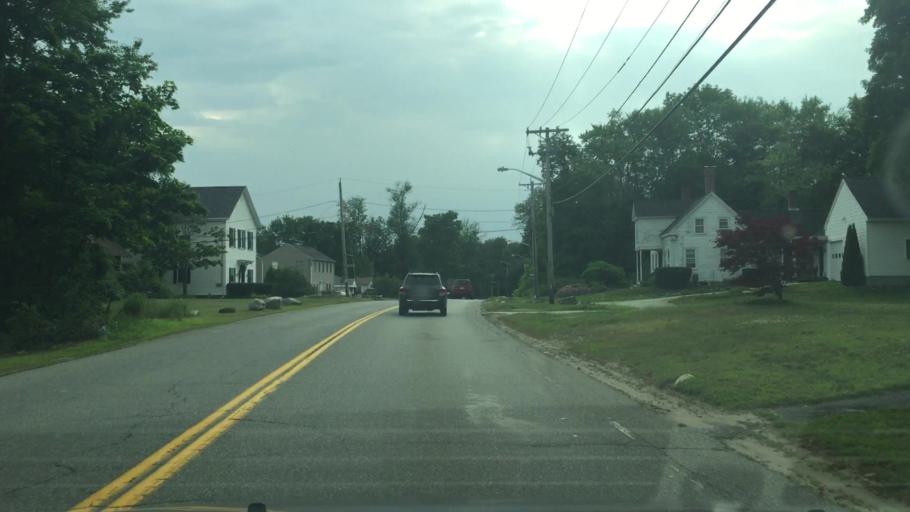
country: US
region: New Hampshire
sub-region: Rockingham County
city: Salem
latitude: 42.7874
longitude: -71.1624
